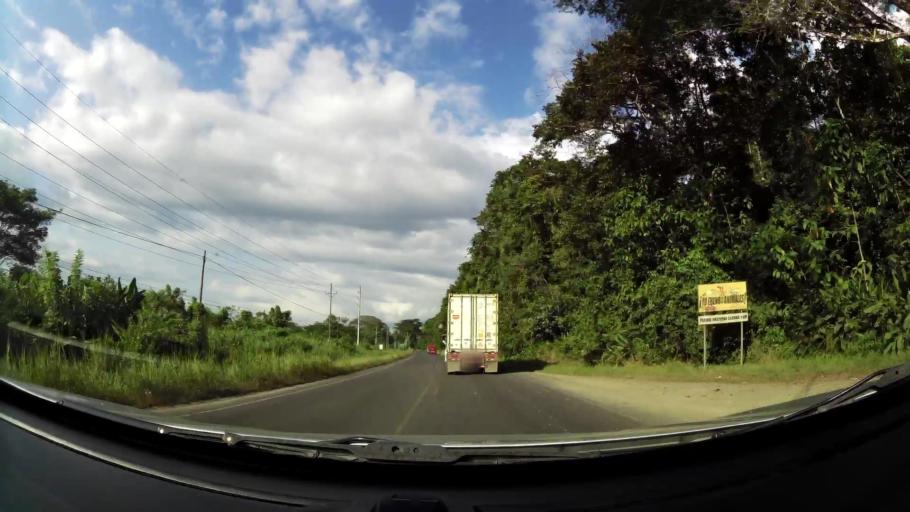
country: CR
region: Puntarenas
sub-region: Canton de Garabito
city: Jaco
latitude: 9.7735
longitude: -84.6078
